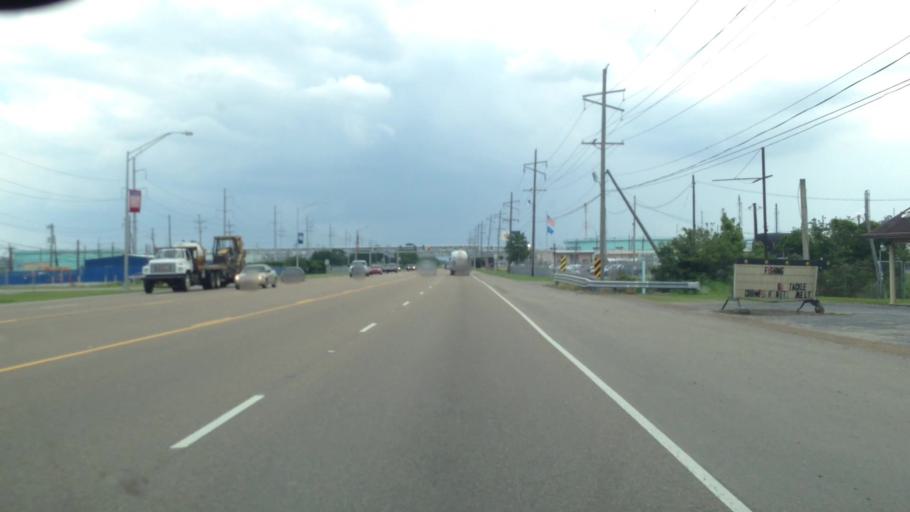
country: US
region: Louisiana
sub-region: Saint Charles Parish
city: Norco
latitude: 30.0143
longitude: -90.4056
